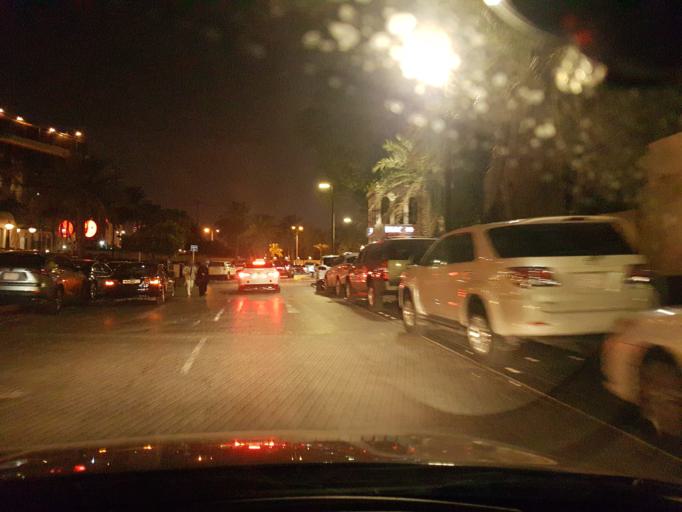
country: BH
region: Manama
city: Manama
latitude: 26.2154
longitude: 50.5926
